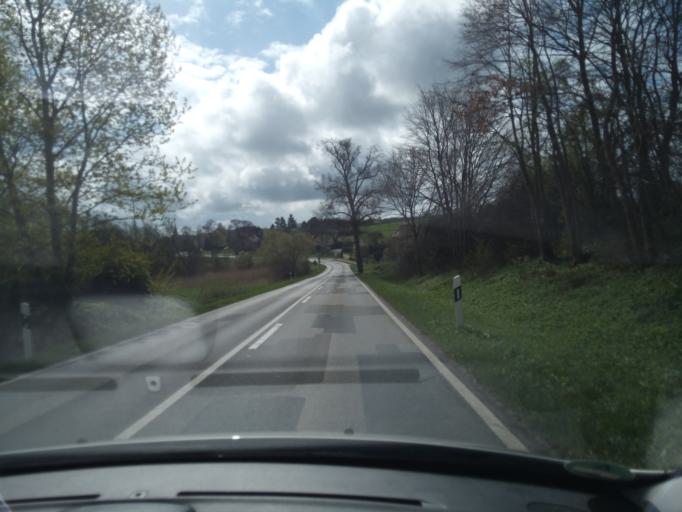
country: DE
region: Mecklenburg-Vorpommern
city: Burg Stargard
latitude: 53.5027
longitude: 13.2972
